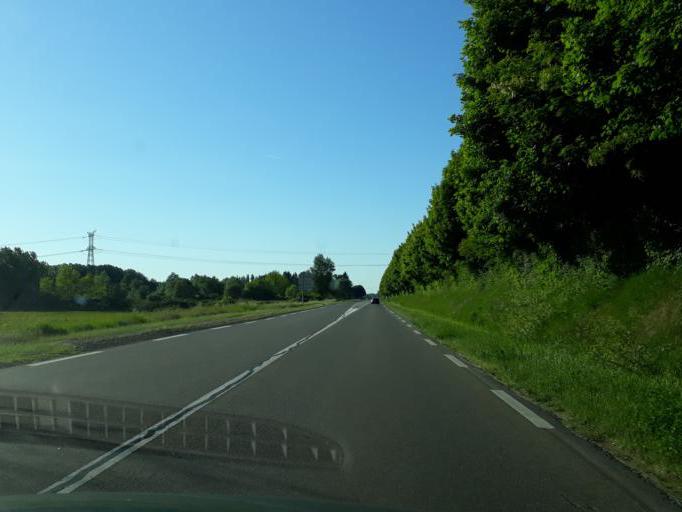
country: FR
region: Bourgogne
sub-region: Departement de la Nievre
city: Neuvy-sur-Loire
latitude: 47.5283
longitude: 2.8690
